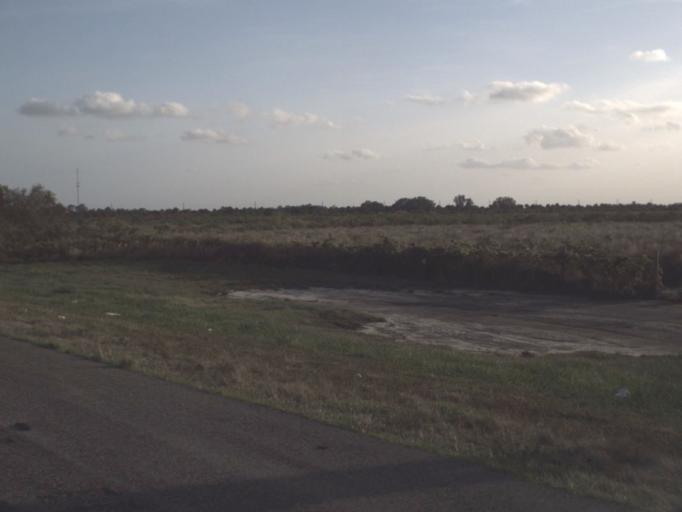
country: US
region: Florida
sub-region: Brevard County
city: Titusville
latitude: 28.5628
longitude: -80.8517
